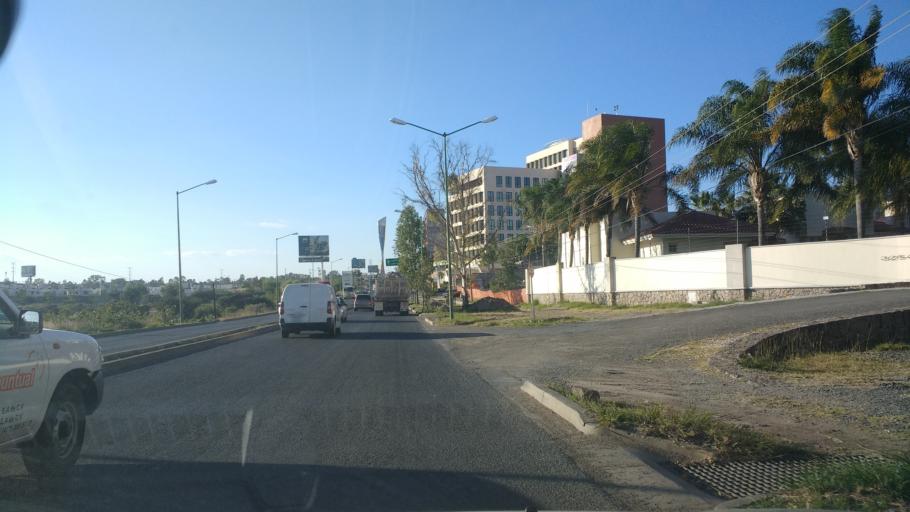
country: MX
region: Guanajuato
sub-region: Leon
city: La Ermita
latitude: 21.1693
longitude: -101.7314
